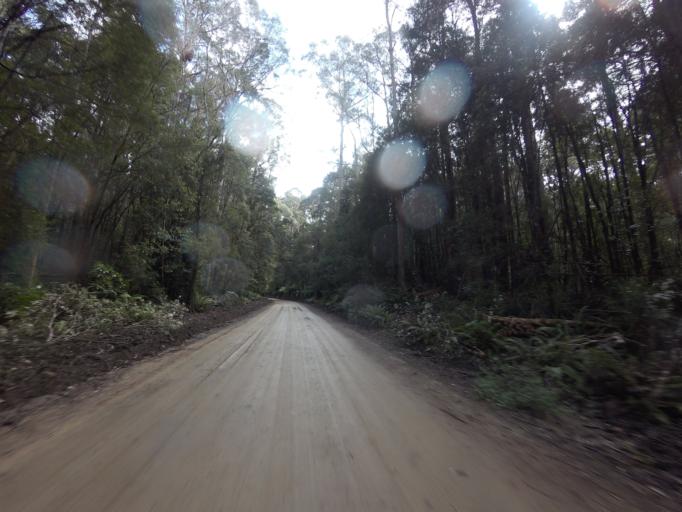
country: AU
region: Tasmania
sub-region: Huon Valley
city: Geeveston
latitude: -43.3883
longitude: 146.8501
